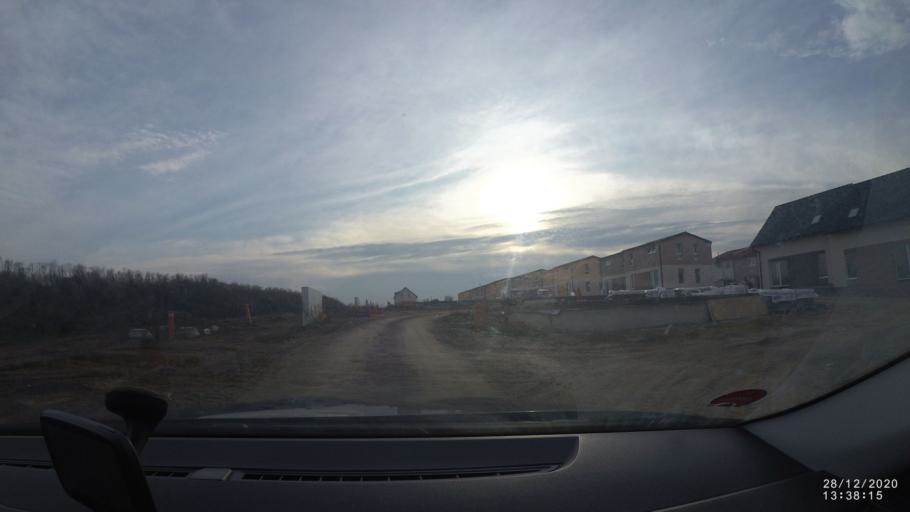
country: CZ
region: Central Bohemia
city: Nehvizdy
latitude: 50.1317
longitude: 14.7429
